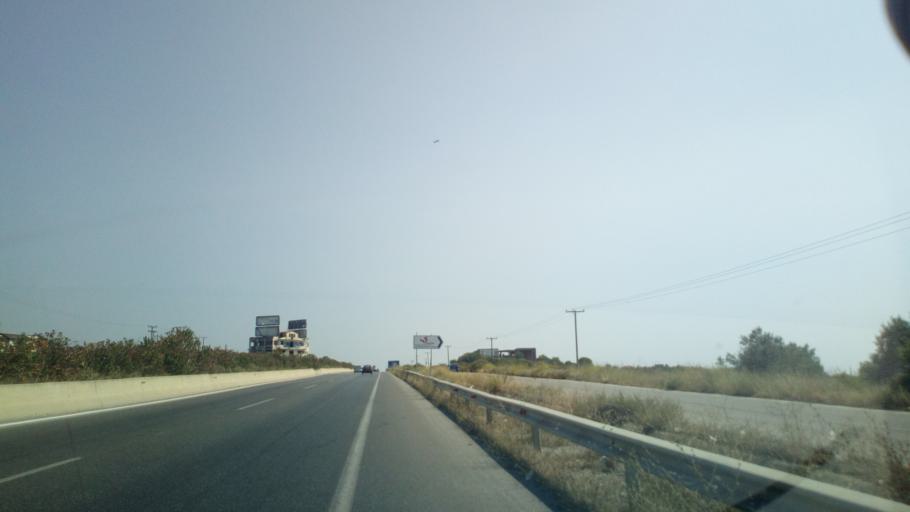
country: GR
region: Central Macedonia
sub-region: Nomos Chalkidikis
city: Lakkoma
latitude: 40.3582
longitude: 23.0535
